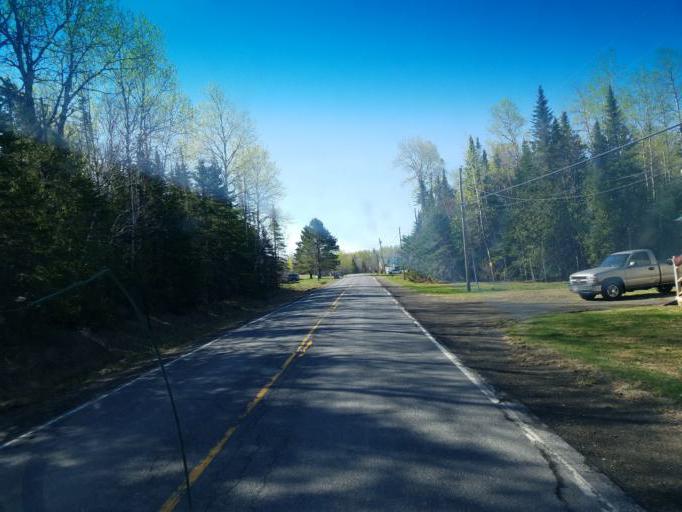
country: US
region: Maine
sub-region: Aroostook County
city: Caribou
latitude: 46.8493
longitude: -68.1964
